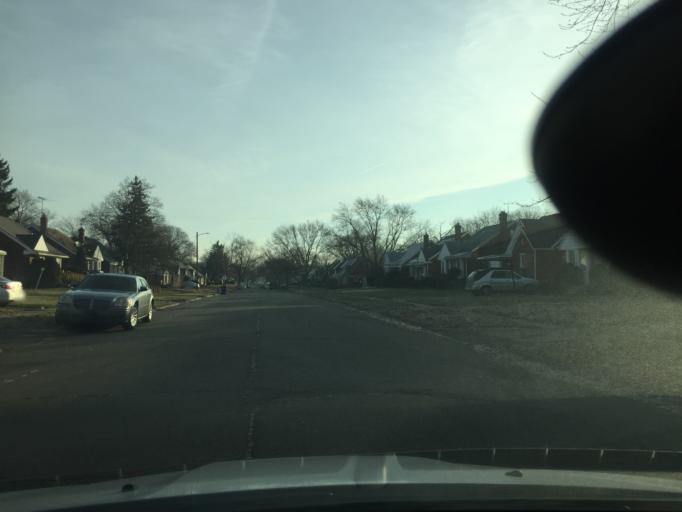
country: US
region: Michigan
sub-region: Macomb County
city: Eastpointe
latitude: 42.4419
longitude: -82.9572
